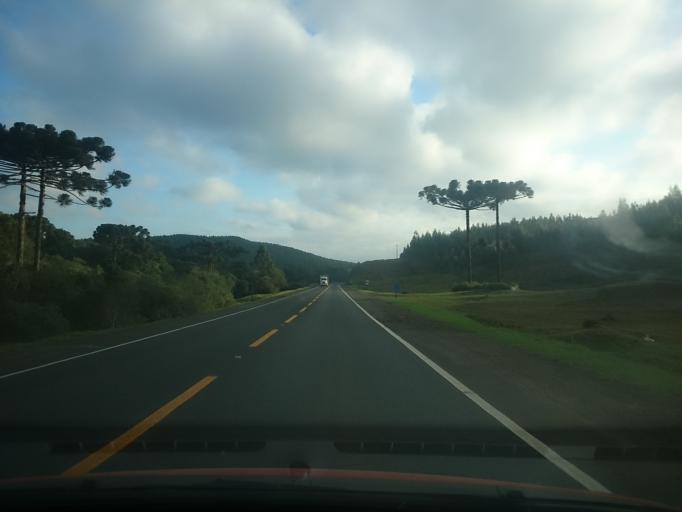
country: BR
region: Santa Catarina
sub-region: Lages
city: Lages
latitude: -28.0479
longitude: -50.5683
